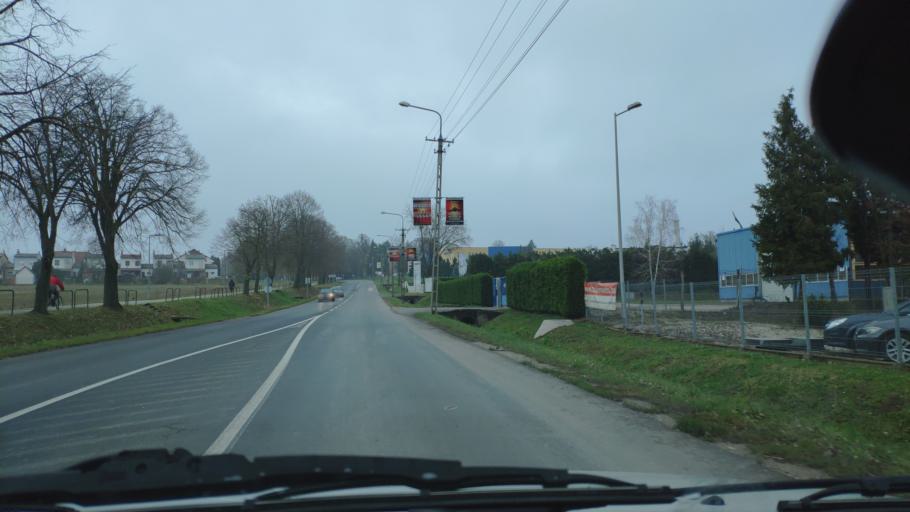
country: HU
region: Zala
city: Nagykanizsa
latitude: 46.4509
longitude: 17.0184
